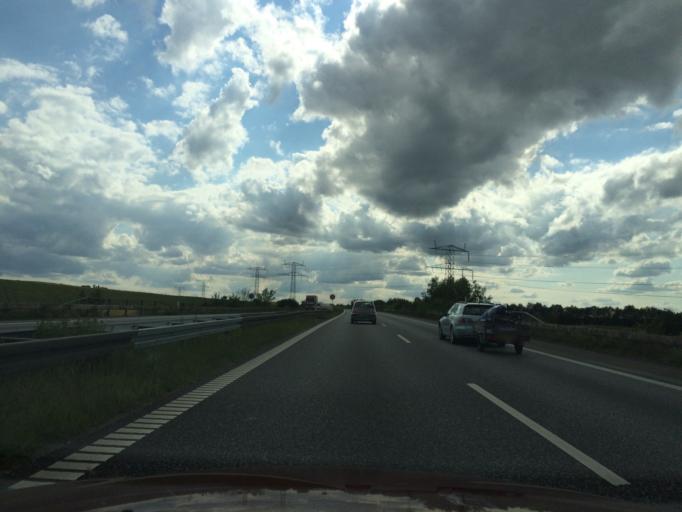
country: DK
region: Central Jutland
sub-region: Favrskov Kommune
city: Soften
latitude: 56.2157
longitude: 10.1022
